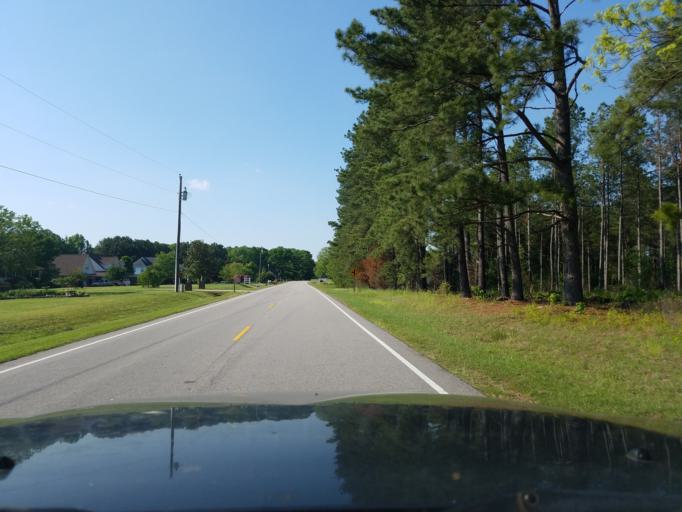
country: US
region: North Carolina
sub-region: Vance County
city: Henderson
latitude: 36.3923
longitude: -78.3681
